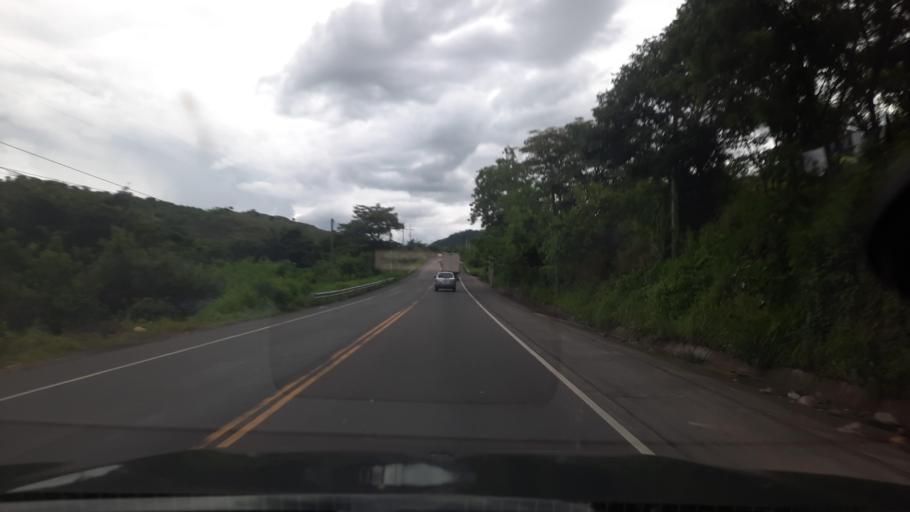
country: HN
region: Choluteca
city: Marcovia
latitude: 13.3638
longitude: -87.2838
